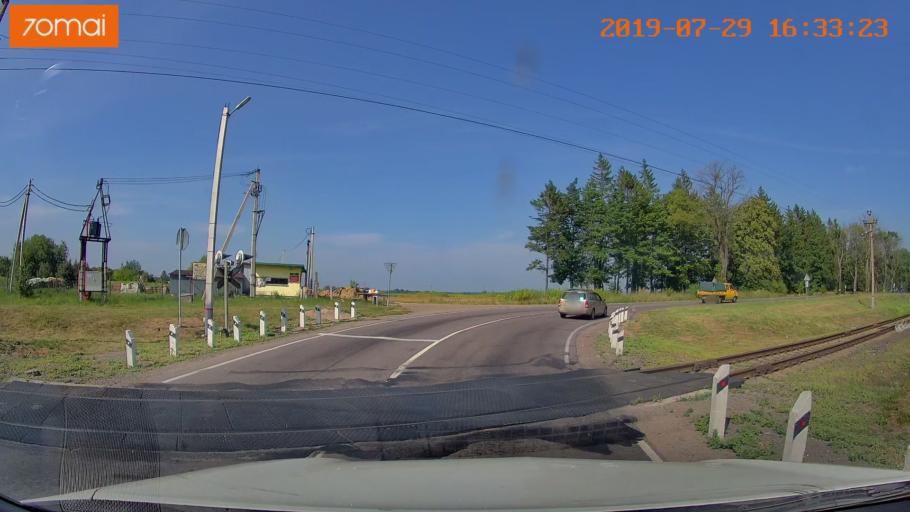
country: RU
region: Kaliningrad
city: Primorsk
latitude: 54.7379
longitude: 20.0372
